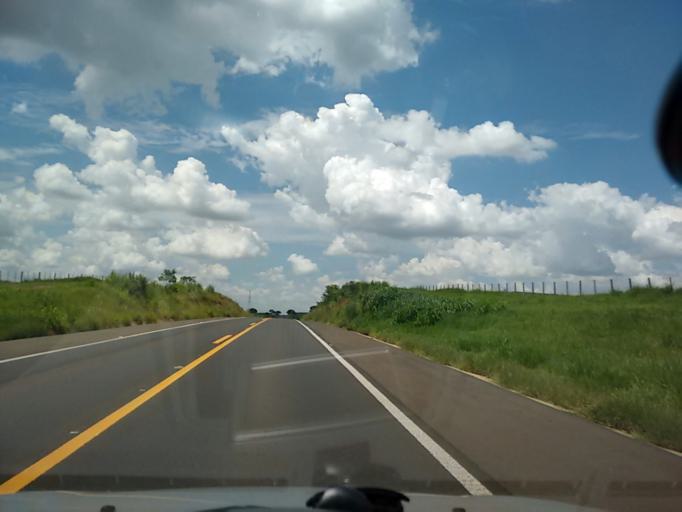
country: BR
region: Sao Paulo
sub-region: Osvaldo Cruz
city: Osvaldo Cruz
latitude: -21.8725
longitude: -50.8566
